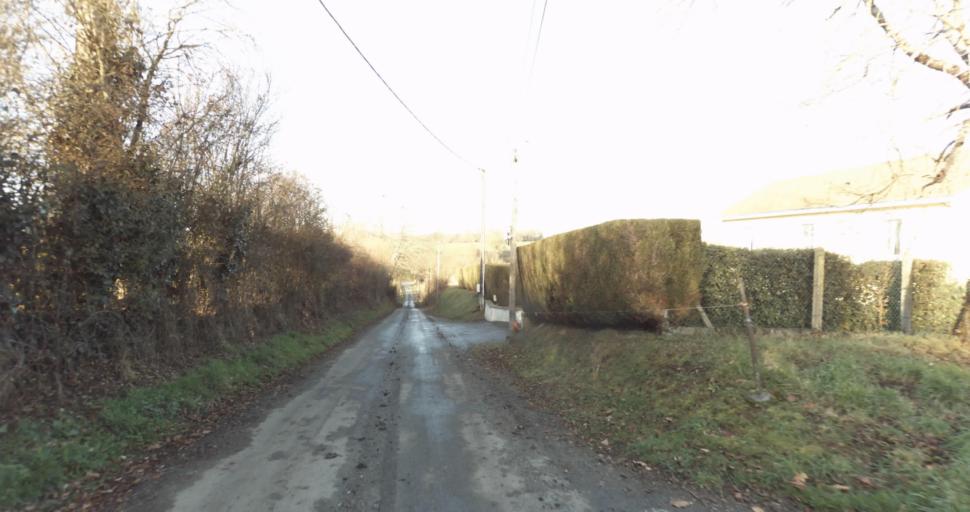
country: FR
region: Limousin
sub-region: Departement de la Haute-Vienne
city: Aixe-sur-Vienne
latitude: 45.7802
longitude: 1.1506
